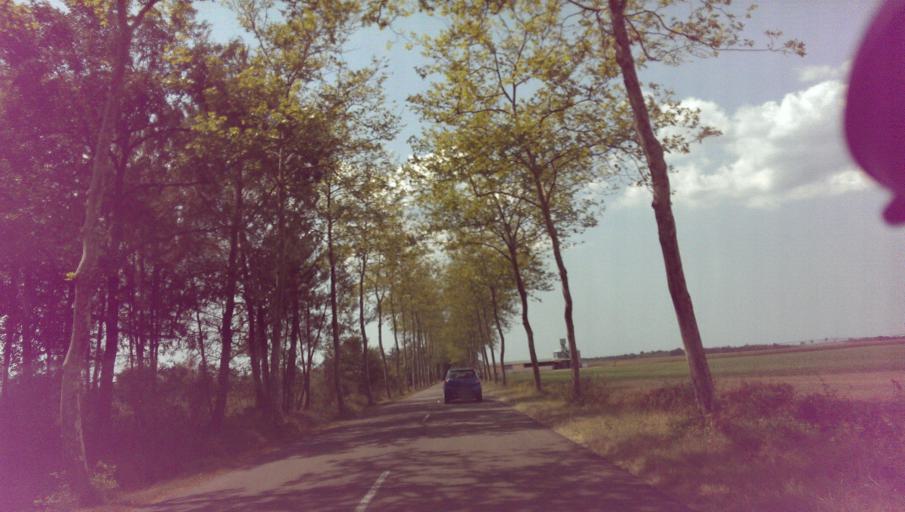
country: FR
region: Aquitaine
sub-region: Departement des Landes
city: Sabres
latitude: 44.1177
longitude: -0.6355
